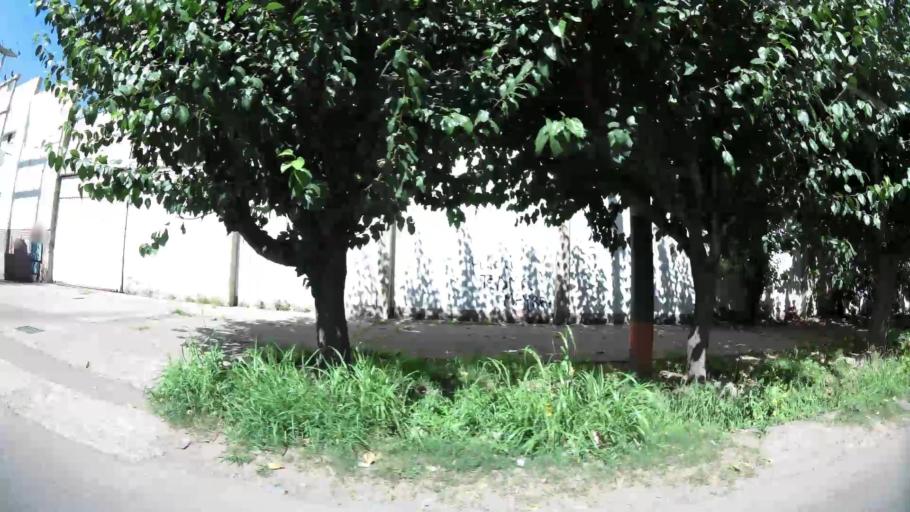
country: AR
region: Mendoza
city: Villa Nueva
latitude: -32.8893
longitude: -68.7828
